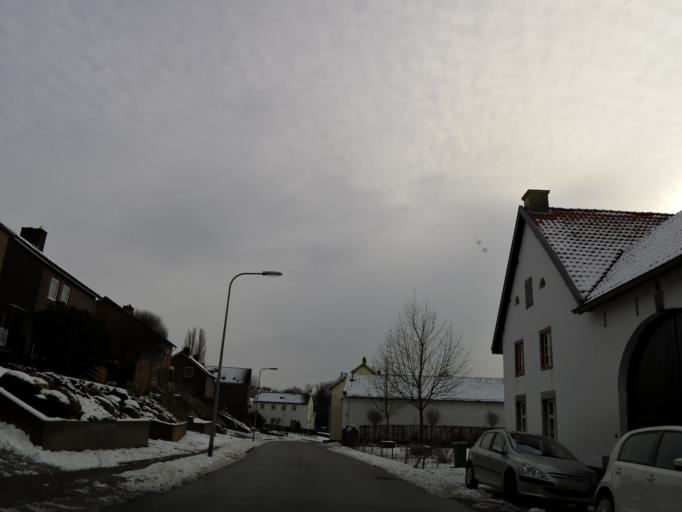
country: NL
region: Limburg
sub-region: Valkenburg aan de Geul
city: Schin op Geul
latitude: 50.8541
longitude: 5.8736
